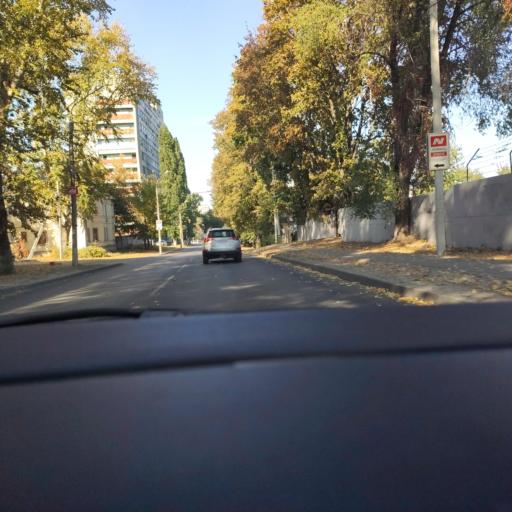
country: RU
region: Voronezj
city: Voronezh
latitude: 51.6887
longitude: 39.1907
